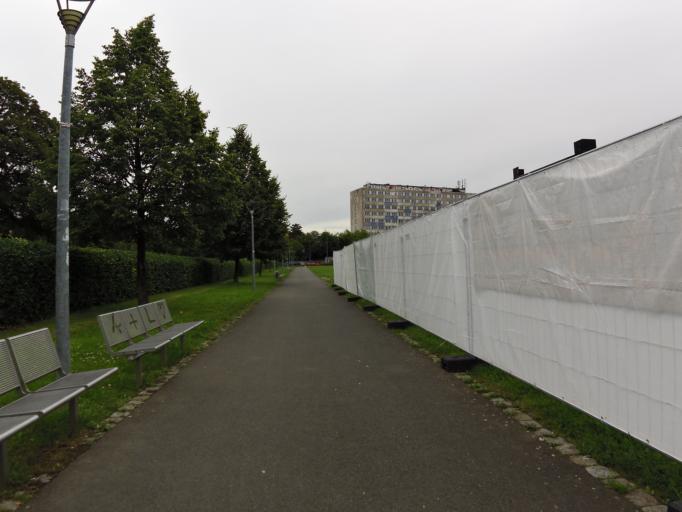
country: DE
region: Thuringia
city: Erfurt
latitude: 50.9893
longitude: 11.0108
